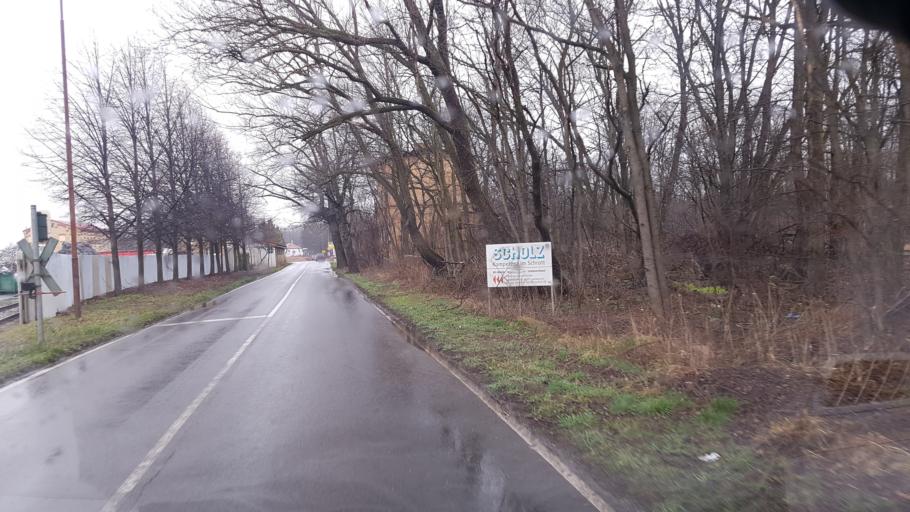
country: DE
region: Brandenburg
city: Lauchhammer
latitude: 51.4964
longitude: 13.8105
